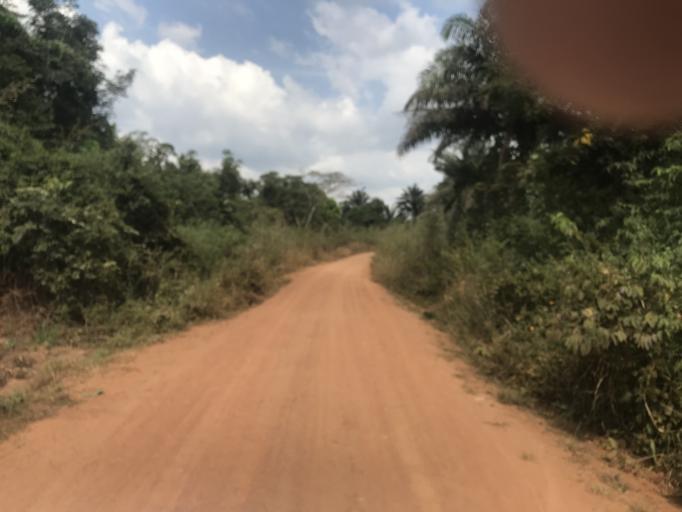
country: NG
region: Osun
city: Inisa
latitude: 7.8887
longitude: 4.3951
